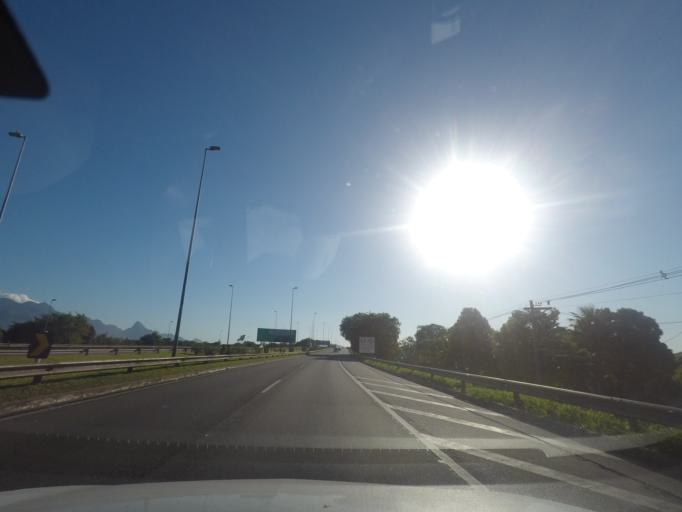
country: BR
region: Rio de Janeiro
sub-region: Petropolis
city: Petropolis
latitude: -22.6477
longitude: -43.2265
